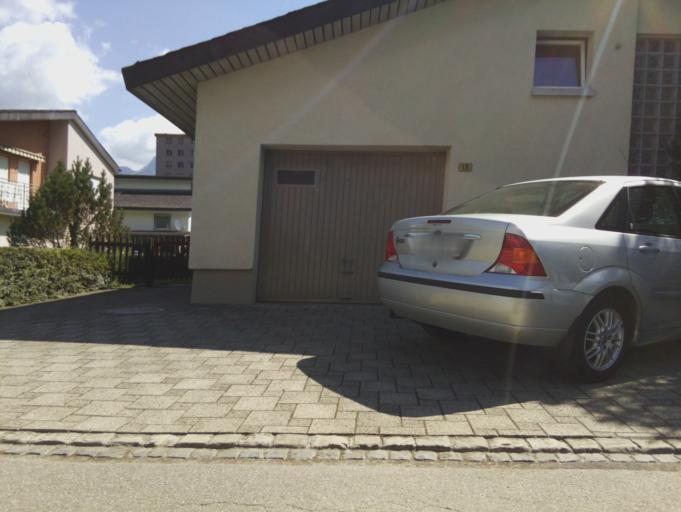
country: CH
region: Glarus
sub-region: Glarus
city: Oberurnen
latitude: 47.1168
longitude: 9.0610
